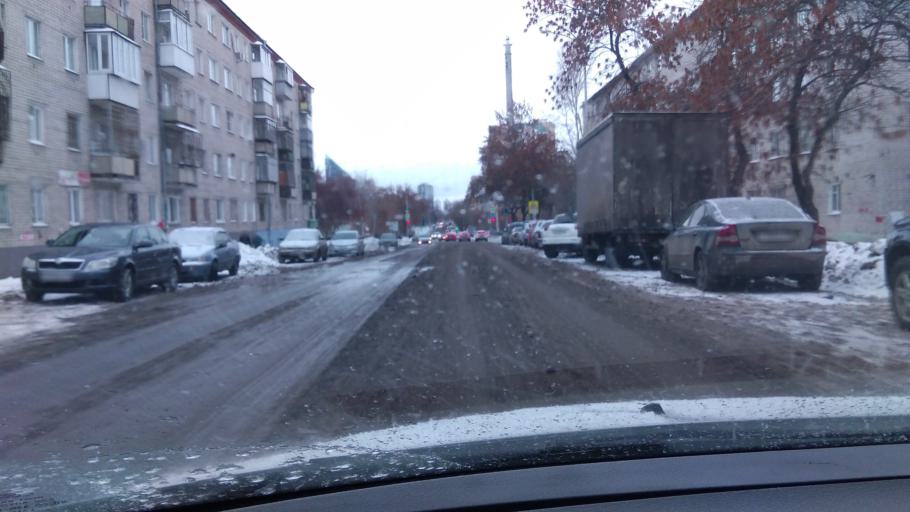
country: RU
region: Sverdlovsk
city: Yekaterinburg
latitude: 56.8144
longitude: 60.6110
